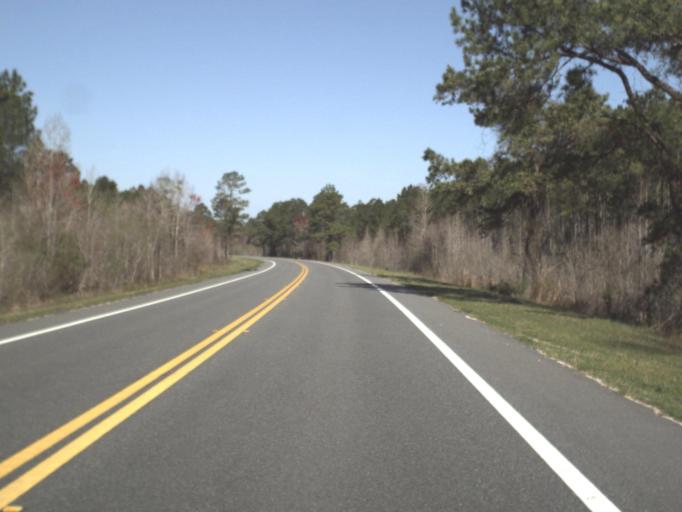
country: US
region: Florida
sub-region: Leon County
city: Woodville
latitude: 30.1818
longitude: -84.0133
